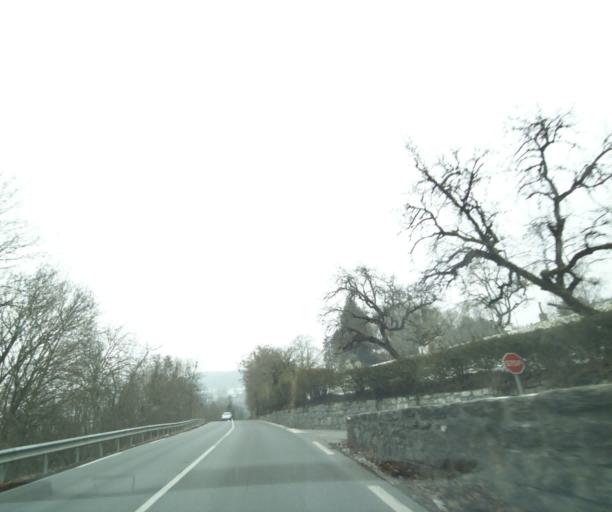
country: FR
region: Rhone-Alpes
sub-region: Departement de la Haute-Savoie
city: Vetraz-Monthoux
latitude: 46.1660
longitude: 6.2407
